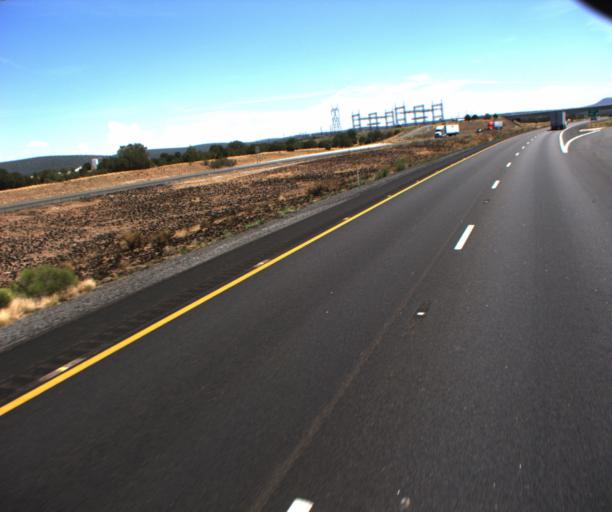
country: US
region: Arizona
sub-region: Mohave County
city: Peach Springs
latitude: 35.1904
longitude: -113.3697
